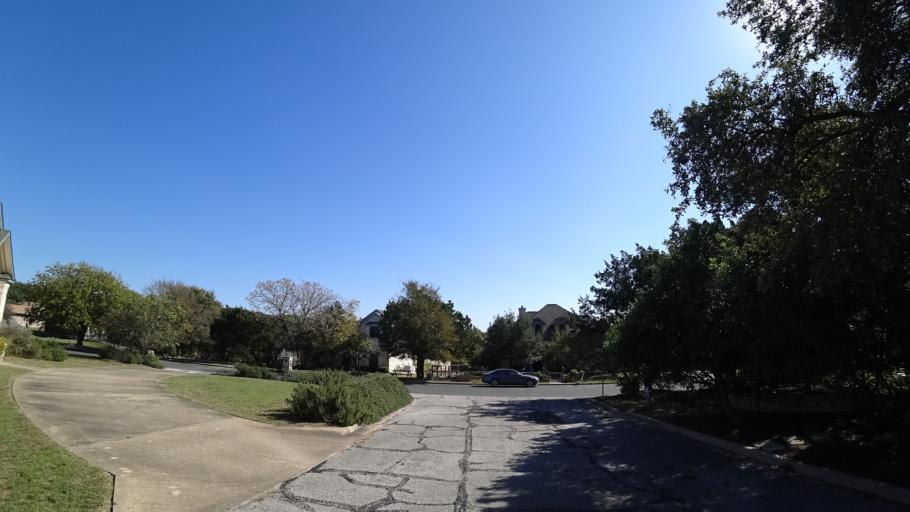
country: US
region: Texas
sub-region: Williamson County
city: Jollyville
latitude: 30.4128
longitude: -97.7553
